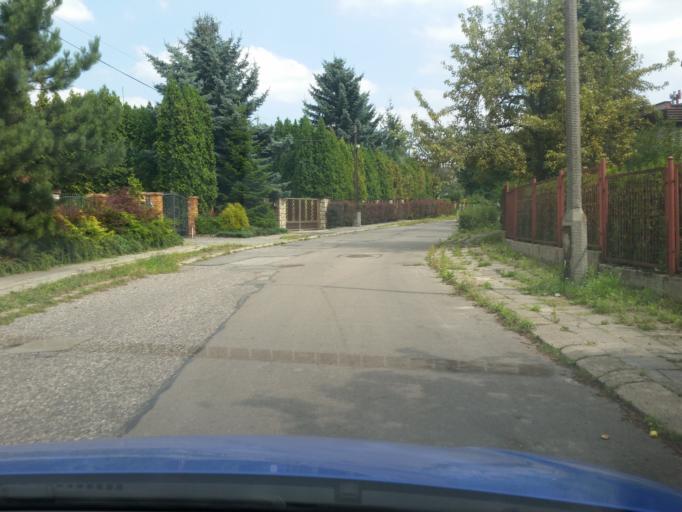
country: PL
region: Silesian Voivodeship
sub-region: Sosnowiec
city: Sosnowiec
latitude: 50.2430
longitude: 19.1038
